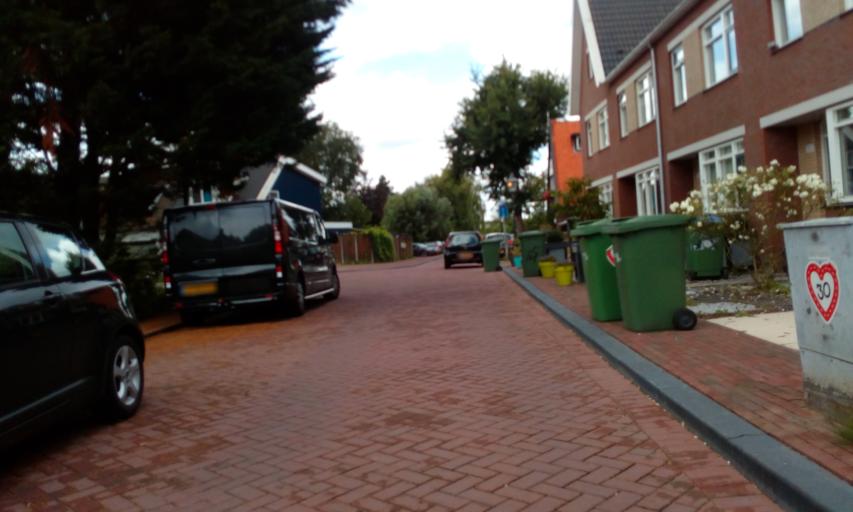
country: NL
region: South Holland
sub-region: Gemeente Barendrecht
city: Barendrecht
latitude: 51.8713
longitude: 4.5433
